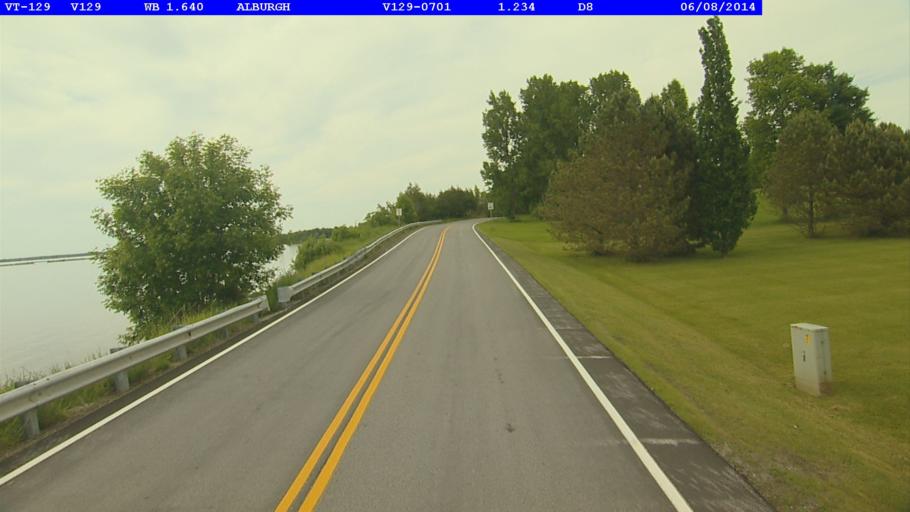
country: US
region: Vermont
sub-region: Grand Isle County
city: North Hero
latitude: 44.8935
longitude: -73.3051
